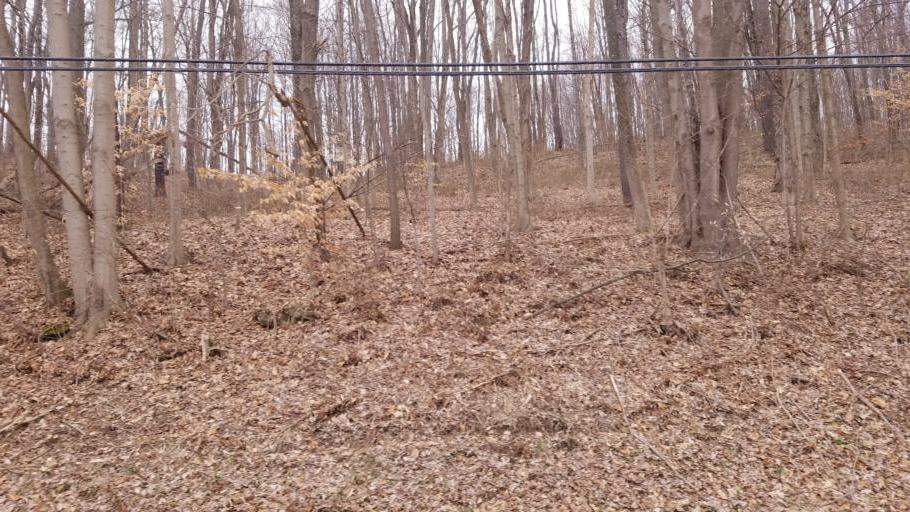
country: US
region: Ohio
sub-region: Sandusky County
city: Bellville
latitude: 40.6350
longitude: -82.5121
